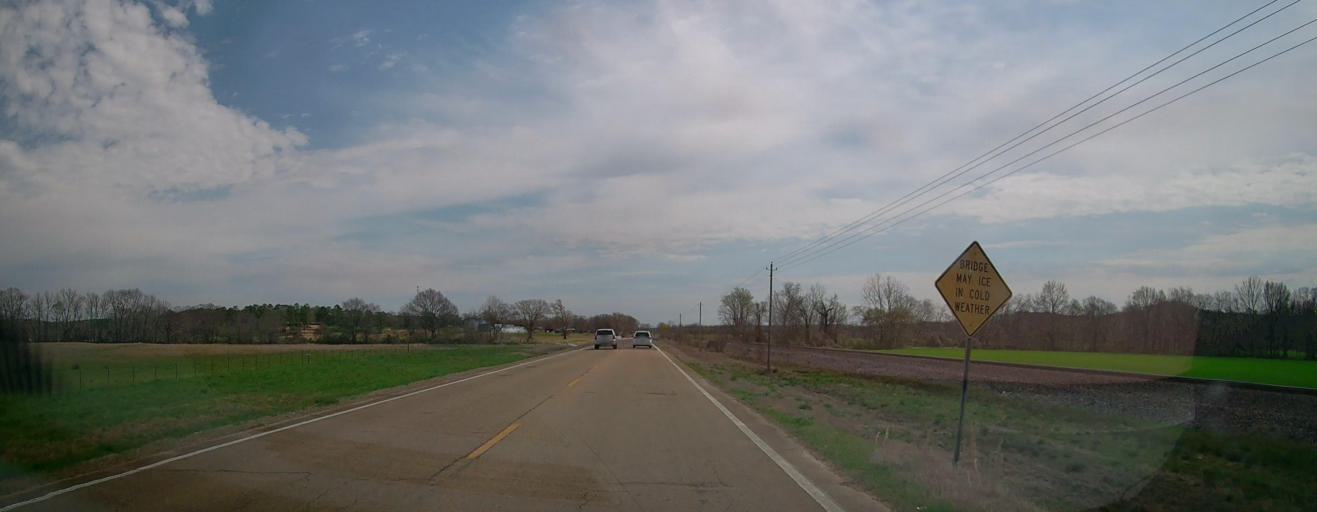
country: US
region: Mississippi
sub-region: Benton County
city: Ashland
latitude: 34.6228
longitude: -89.2402
